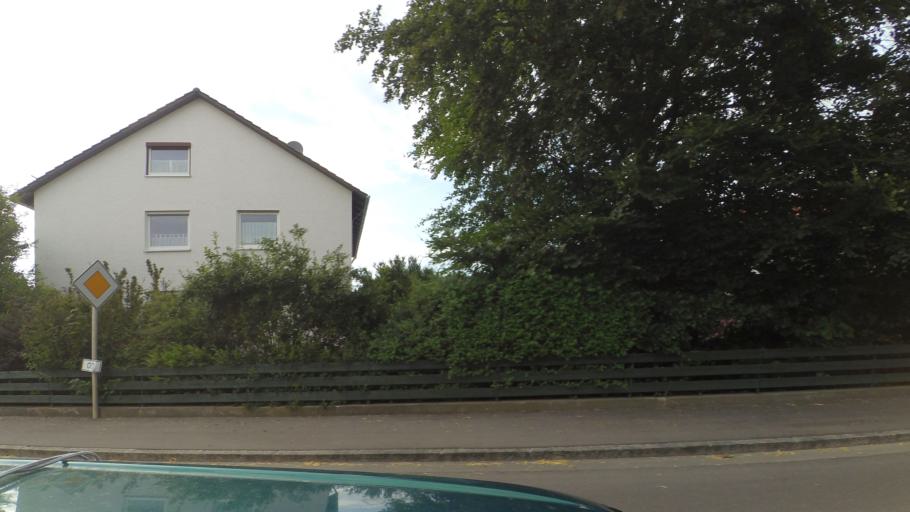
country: DE
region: Bavaria
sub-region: Swabia
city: Hochstadt an der Donau
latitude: 48.6210
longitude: 10.5773
